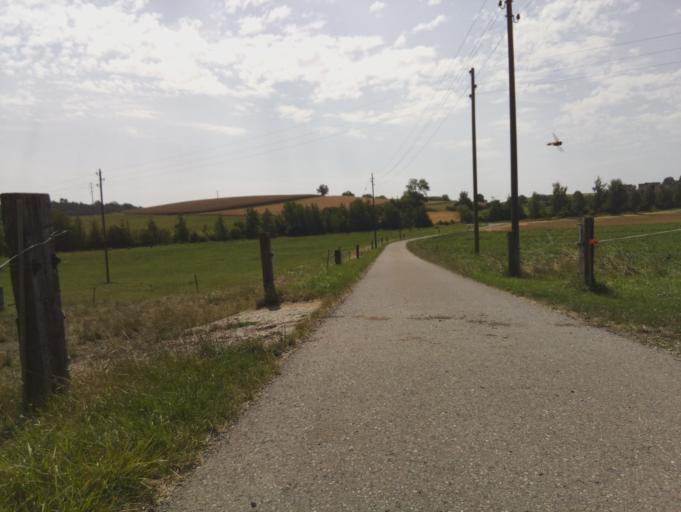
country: CH
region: Zurich
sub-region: Bezirk Andelfingen
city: Grossandelfingen
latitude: 47.5829
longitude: 8.6698
